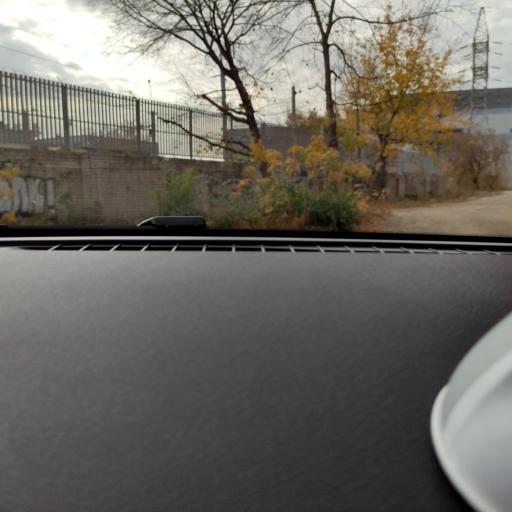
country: RU
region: Samara
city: Samara
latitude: 53.2345
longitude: 50.2029
